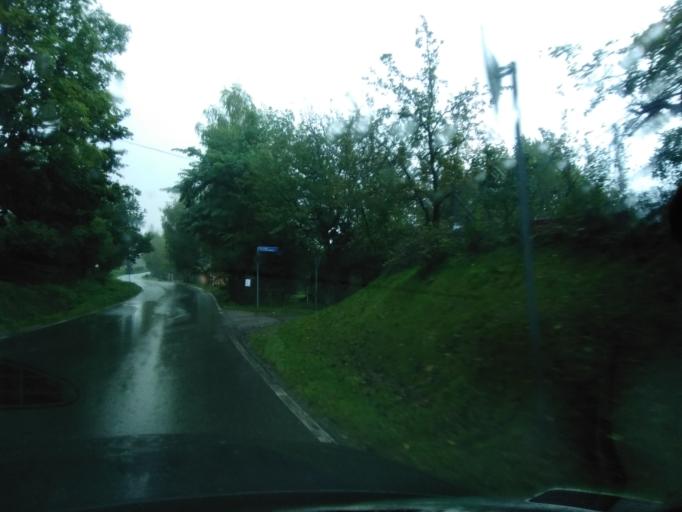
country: PL
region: Subcarpathian Voivodeship
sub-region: Powiat ropczycko-sedziszowski
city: Niedzwiada
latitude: 50.0472
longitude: 21.5375
